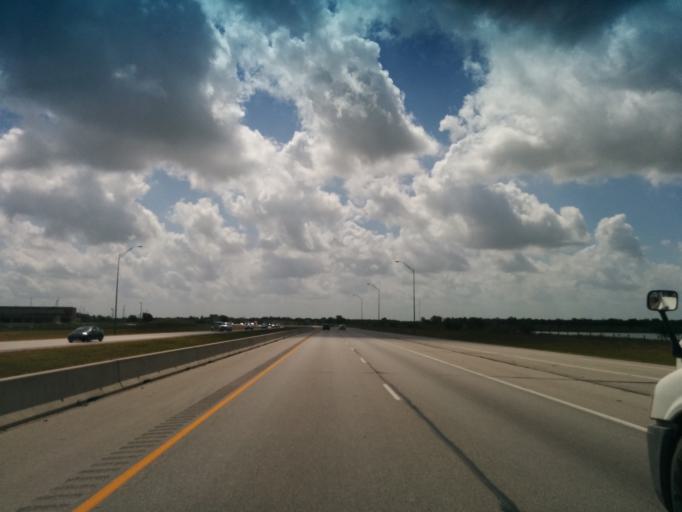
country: US
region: Texas
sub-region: Austin County
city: Sealy
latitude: 29.7612
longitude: -96.1795
